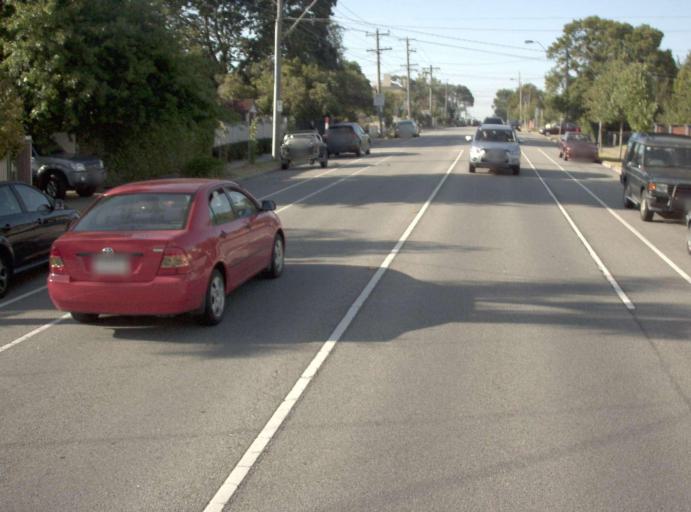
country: AU
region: Victoria
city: Carnegie
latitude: -37.8826
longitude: 145.0678
